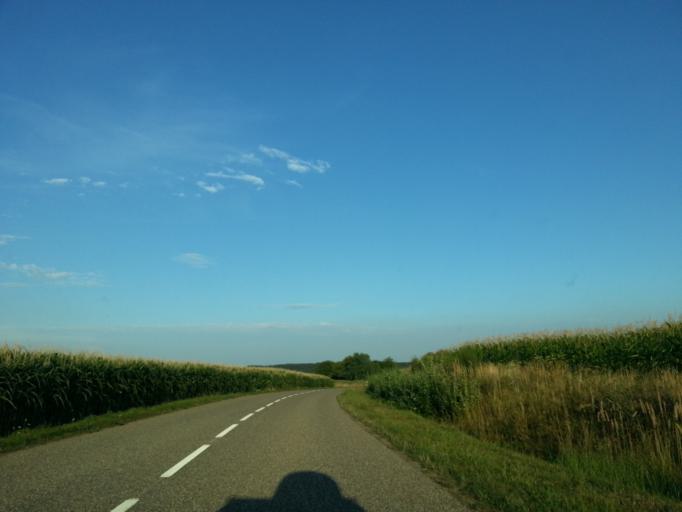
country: FR
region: Alsace
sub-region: Departement du Bas-Rhin
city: Soultz-sous-Forets
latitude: 48.9711
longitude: 7.8758
